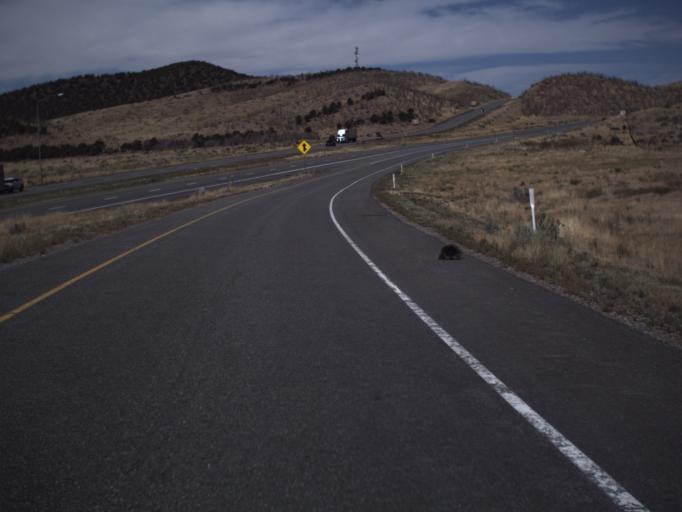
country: US
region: Utah
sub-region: Beaver County
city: Beaver
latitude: 38.6196
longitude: -112.6091
